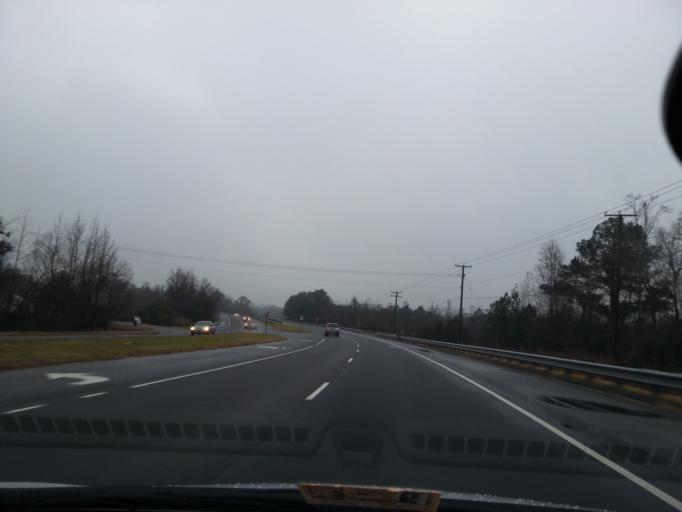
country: US
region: North Carolina
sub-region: Currituck County
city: Moyock
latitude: 36.5698
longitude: -76.2000
